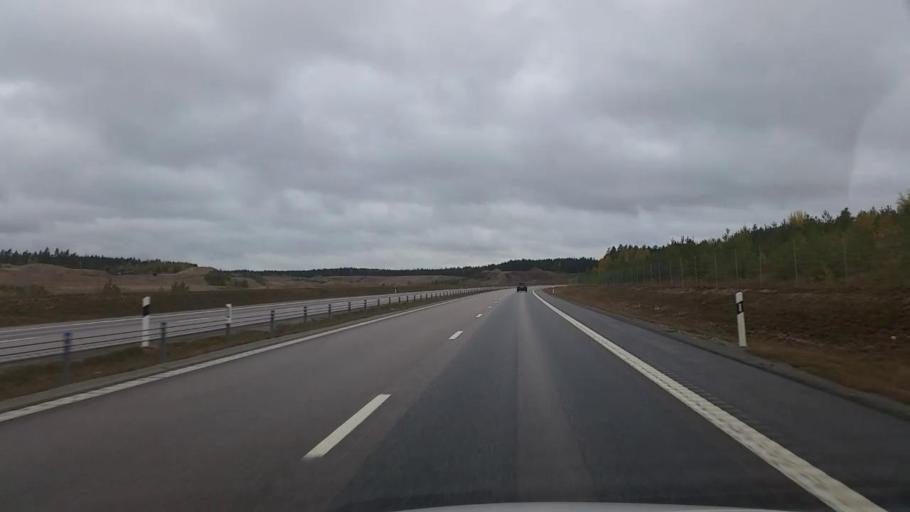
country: SE
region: Uppsala
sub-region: Osthammars Kommun
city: Bjorklinge
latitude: 60.1137
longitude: 17.5525
